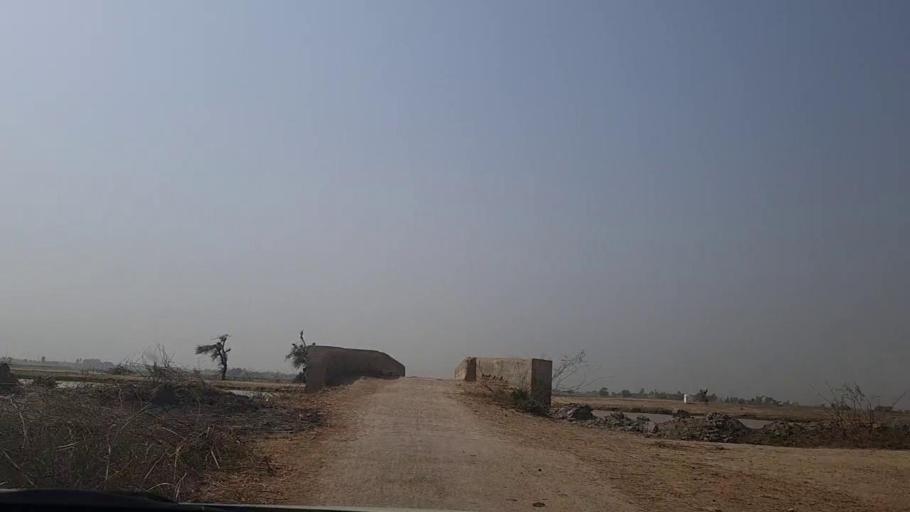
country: PK
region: Sindh
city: Pithoro
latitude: 25.5498
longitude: 69.2136
